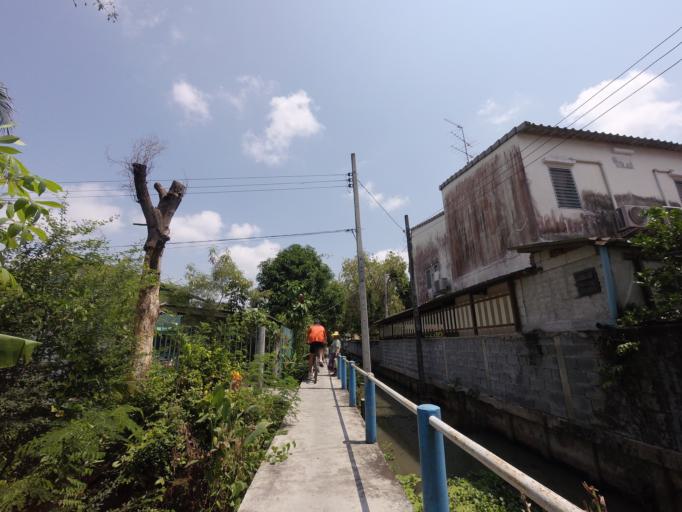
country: TH
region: Bangkok
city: Chom Thong
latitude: 13.6540
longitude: 100.4845
